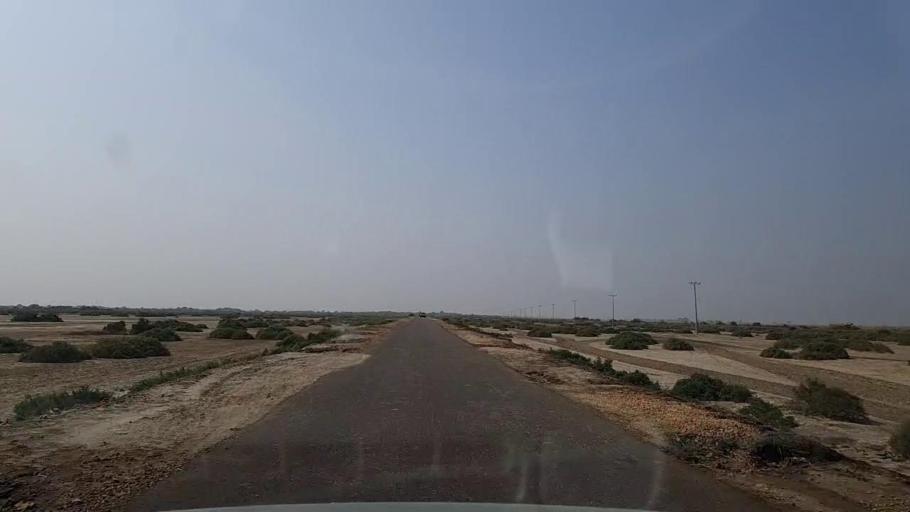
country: PK
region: Sindh
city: Mirpur Sakro
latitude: 24.5288
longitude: 67.5746
